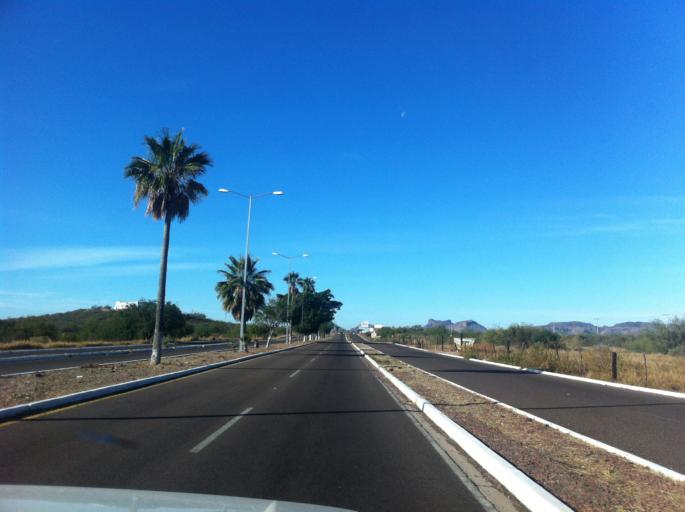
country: MX
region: Sonora
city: Heroica Guaymas
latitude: 27.9784
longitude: -110.9730
